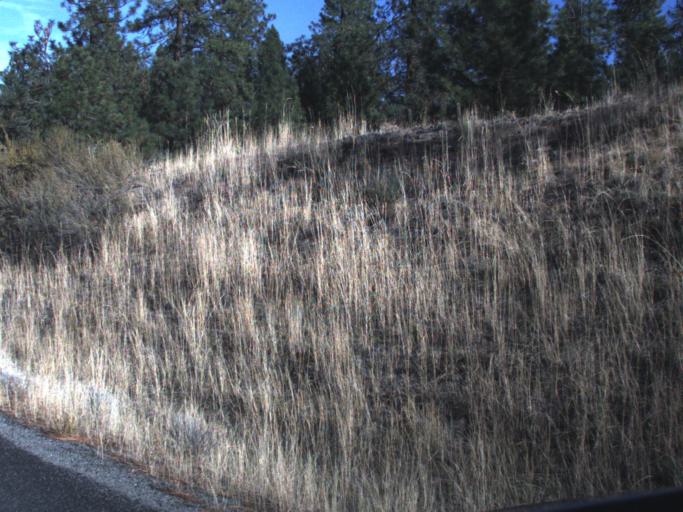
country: US
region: Washington
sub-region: Lincoln County
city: Davenport
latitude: 47.9139
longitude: -118.3324
